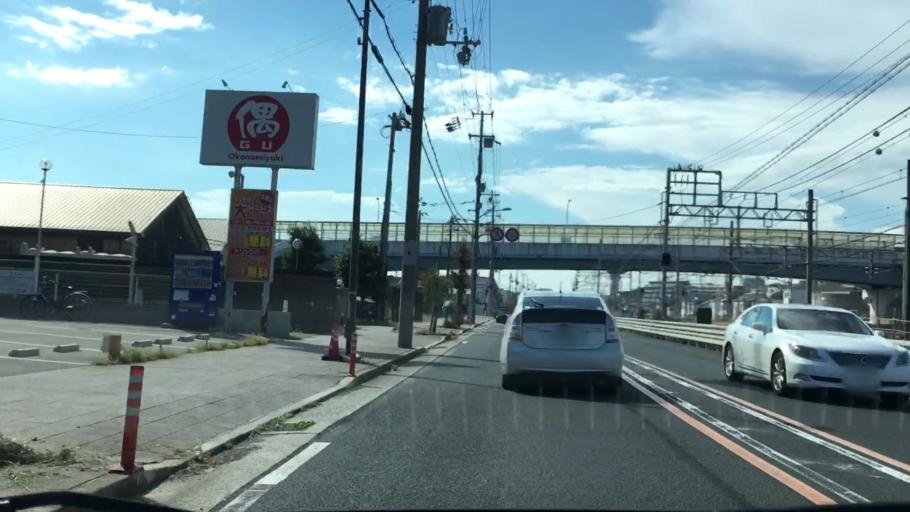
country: JP
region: Hyogo
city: Akashi
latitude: 34.6449
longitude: 135.0131
